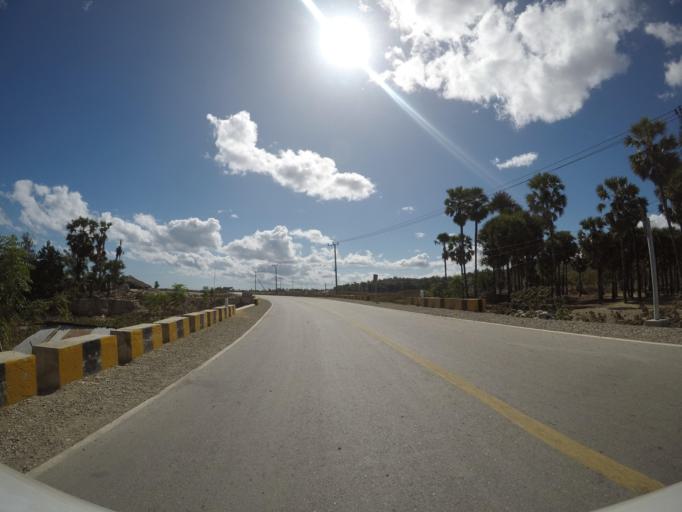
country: TL
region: Baucau
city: Baucau
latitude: -8.4843
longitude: 126.5670
